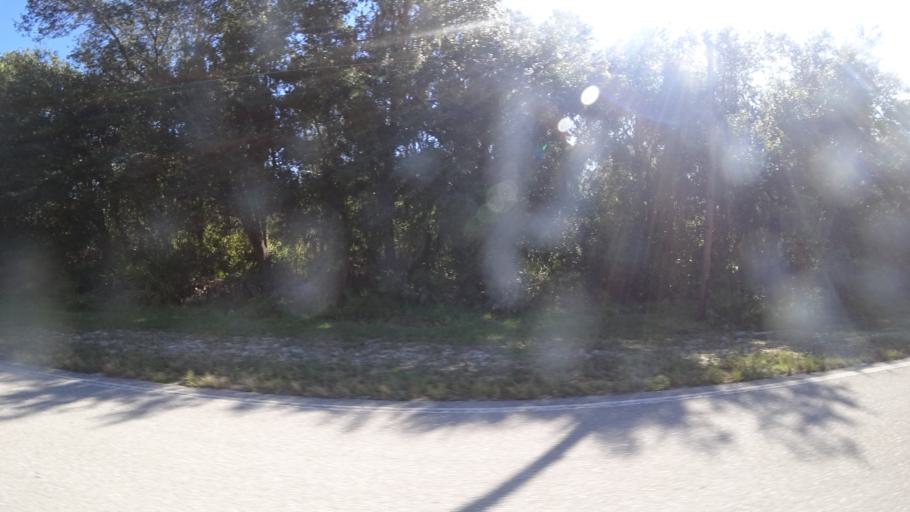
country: US
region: Florida
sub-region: Hillsborough County
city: Wimauma
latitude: 27.6362
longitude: -82.2925
